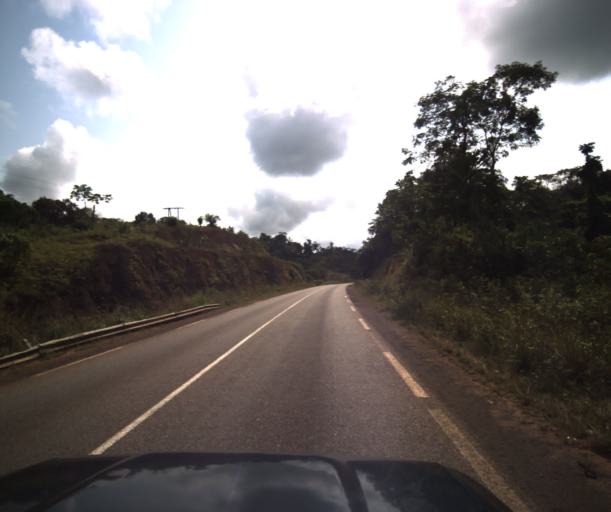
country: CM
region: Littoral
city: Edea
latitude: 3.8042
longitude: 10.2296
